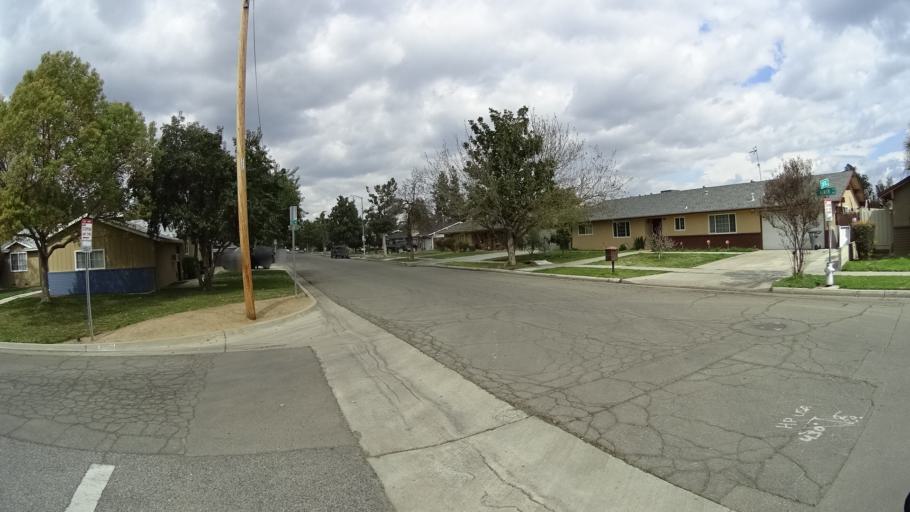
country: US
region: California
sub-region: Fresno County
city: Clovis
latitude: 36.8176
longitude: -119.7588
